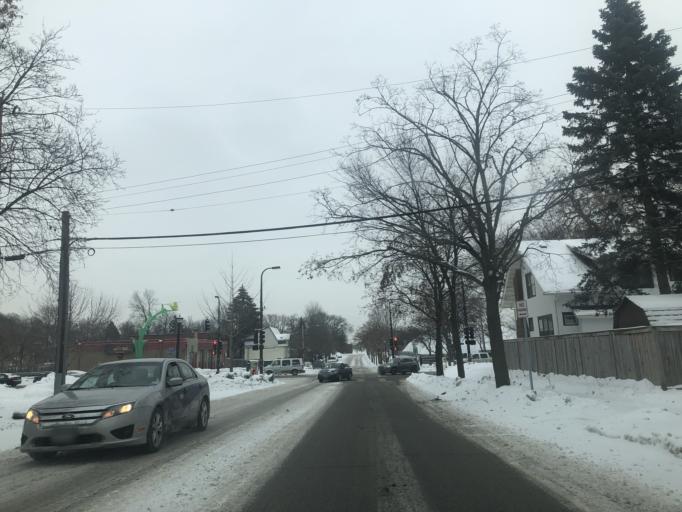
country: US
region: Minnesota
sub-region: Hennepin County
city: Richfield
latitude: 44.9305
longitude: -93.2787
